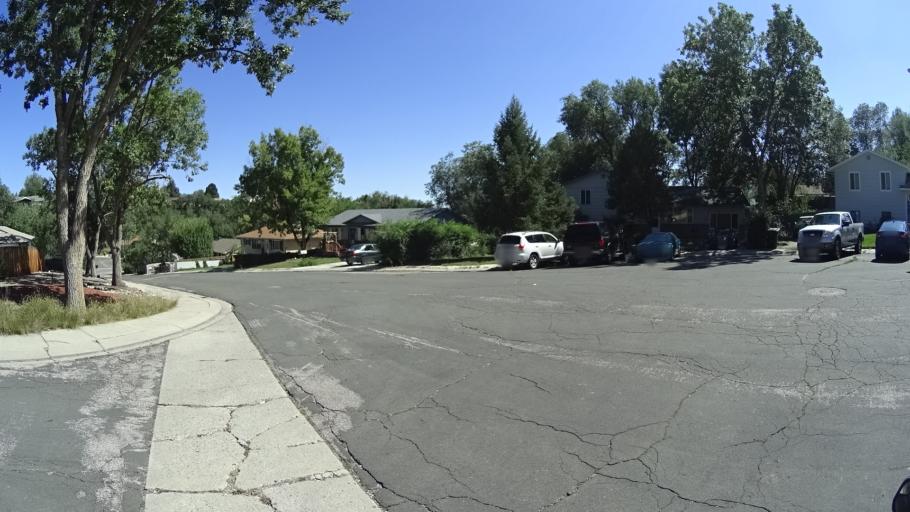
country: US
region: Colorado
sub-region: El Paso County
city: Colorado Springs
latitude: 38.8581
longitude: -104.8582
